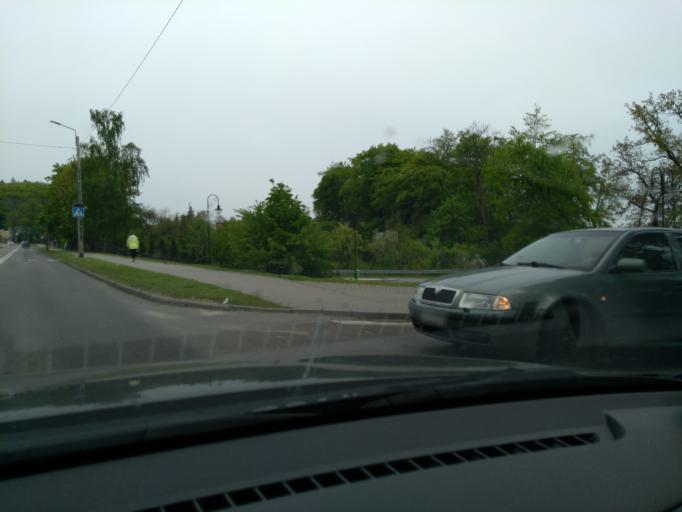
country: PL
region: Pomeranian Voivodeship
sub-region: Powiat kartuski
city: Kartuzy
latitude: 54.3357
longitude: 18.1896
